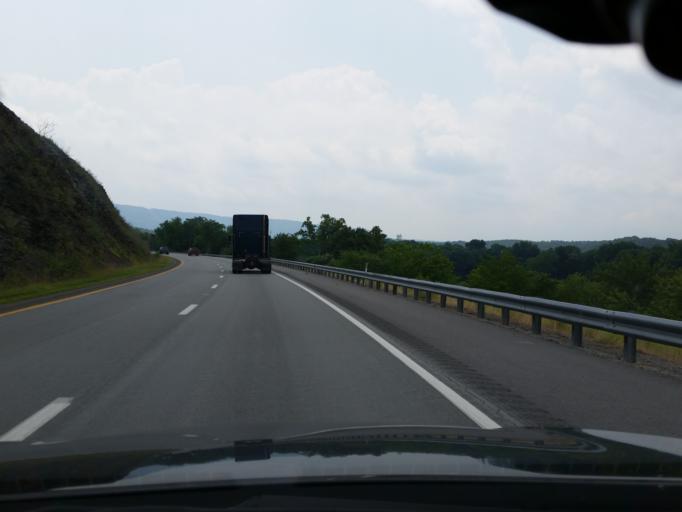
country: US
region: Pennsylvania
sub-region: Perry County
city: Duncannon
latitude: 40.4546
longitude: -77.0245
